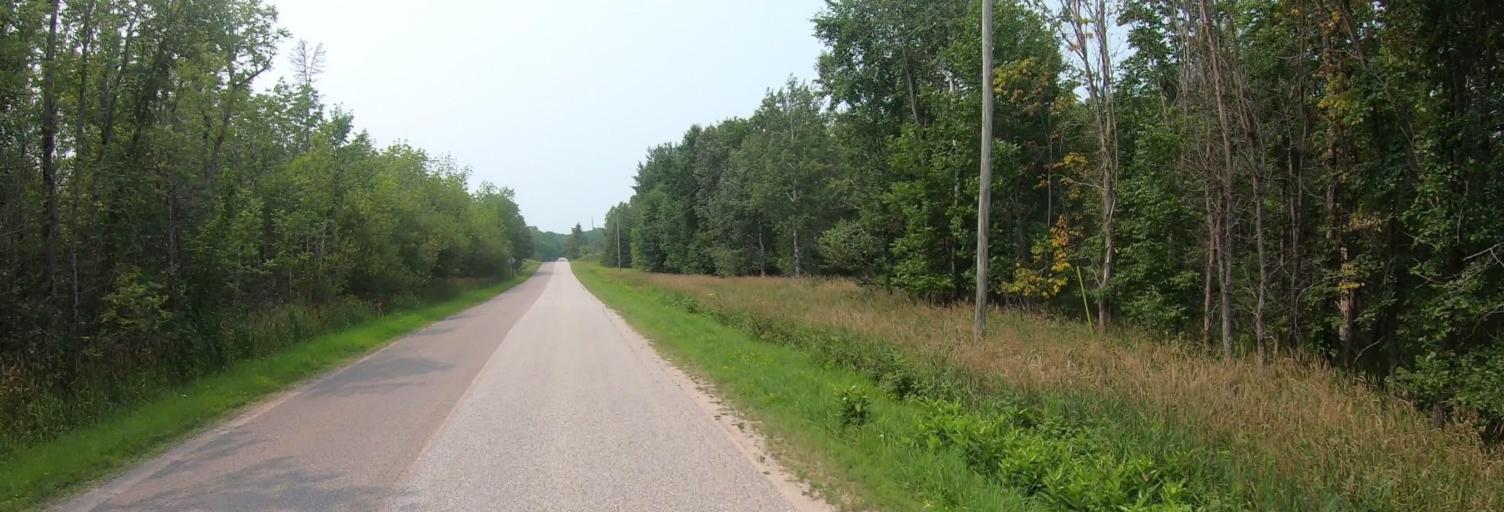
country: CA
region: Ontario
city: Thessalon
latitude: 46.0315
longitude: -83.6668
